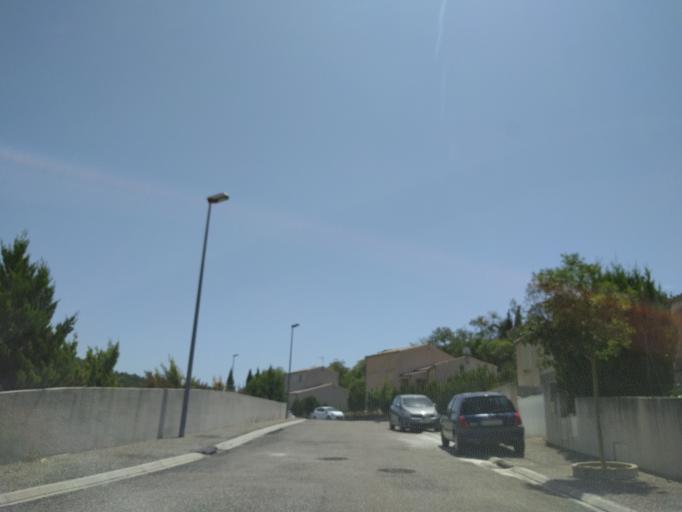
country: FR
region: Languedoc-Roussillon
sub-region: Departement de l'Aude
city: Palaja
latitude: 43.2037
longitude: 2.3967
